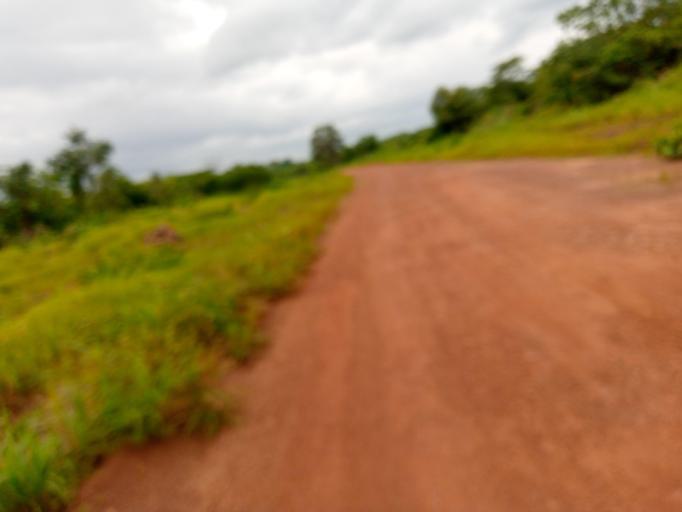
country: SL
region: Southern Province
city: Moyamba
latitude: 8.0962
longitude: -12.4451
